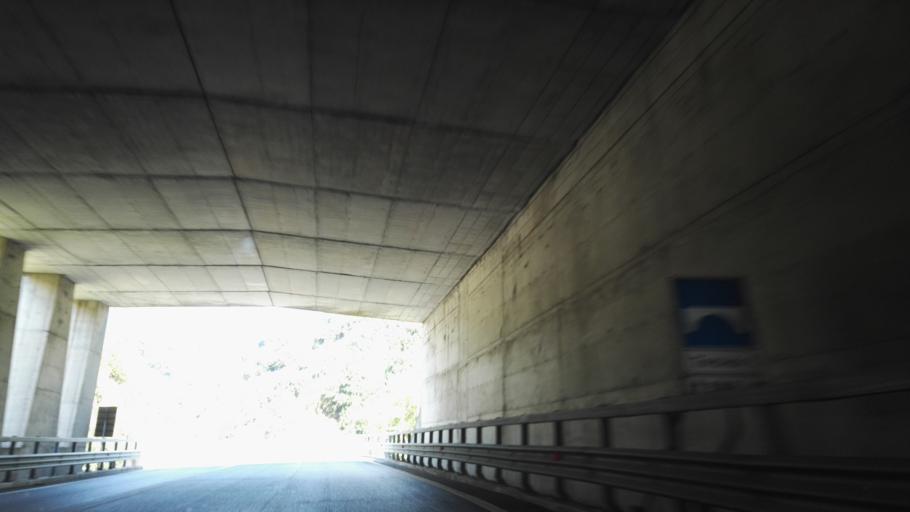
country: IT
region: Calabria
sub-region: Provincia di Reggio Calabria
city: Amato
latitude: 38.3705
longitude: 16.1822
